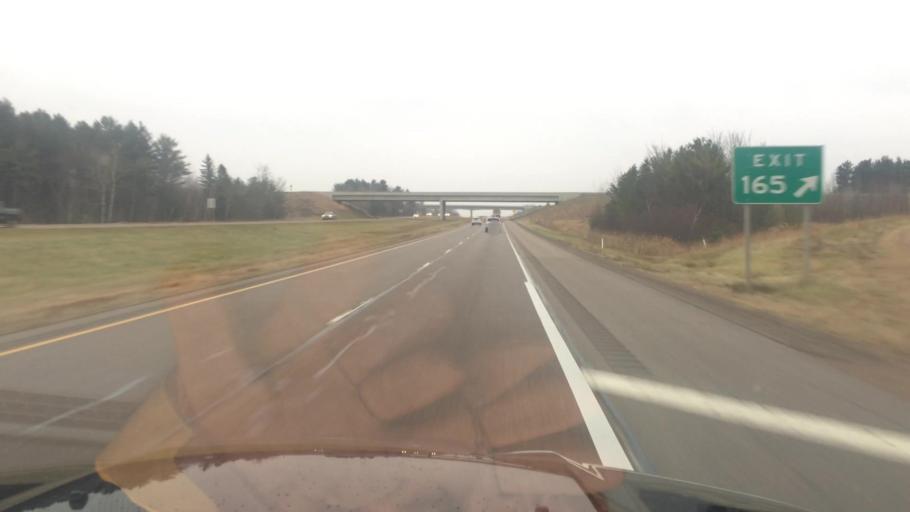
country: US
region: Wisconsin
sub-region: Portage County
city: Stevens Point
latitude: 44.6002
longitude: -89.6170
